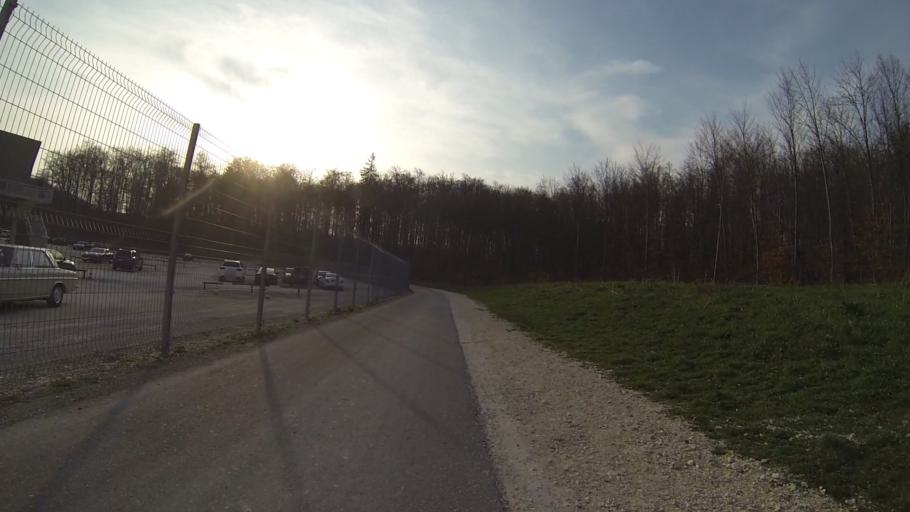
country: DE
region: Baden-Wuerttemberg
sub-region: Regierungsbezirk Stuttgart
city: Heidenheim an der Brenz
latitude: 48.6698
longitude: 10.1397
